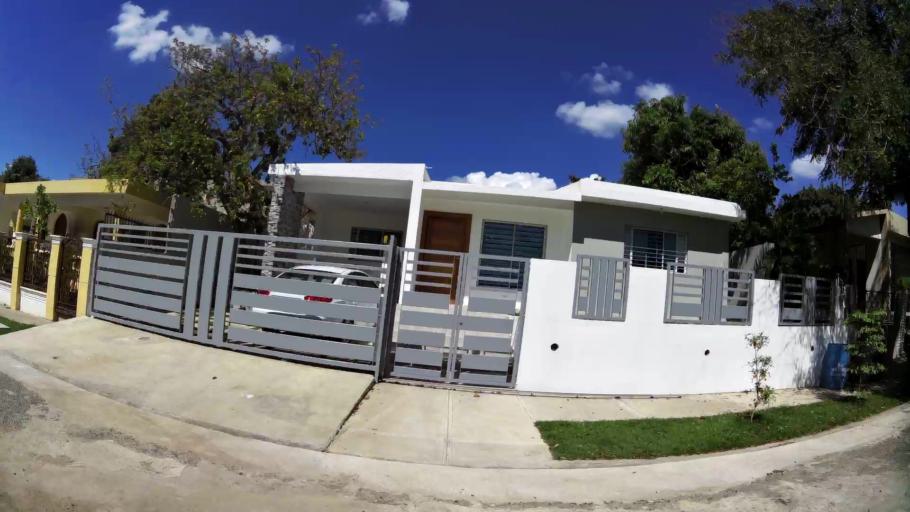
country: DO
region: Santiago
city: Santiago de los Caballeros
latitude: 19.4426
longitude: -70.6925
